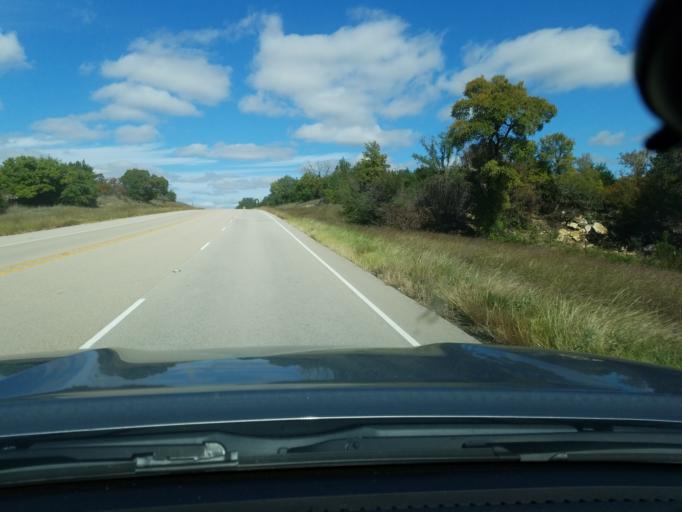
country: US
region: Texas
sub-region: Hamilton County
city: Hamilton
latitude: 31.5864
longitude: -98.1567
